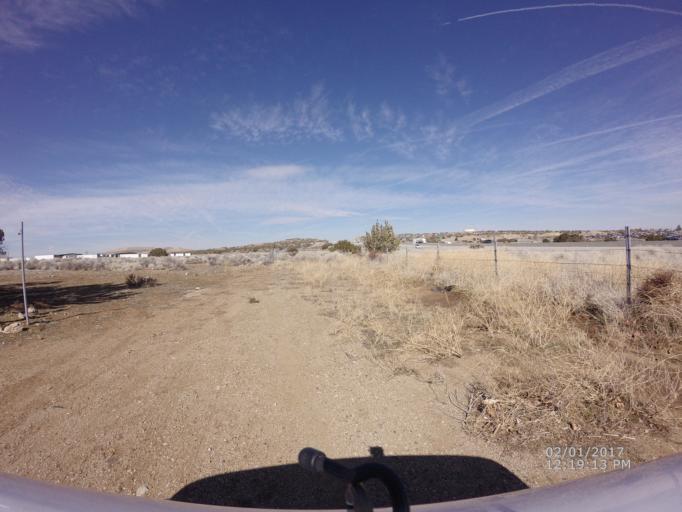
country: US
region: California
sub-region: Los Angeles County
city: Palmdale
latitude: 34.5546
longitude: -118.1326
